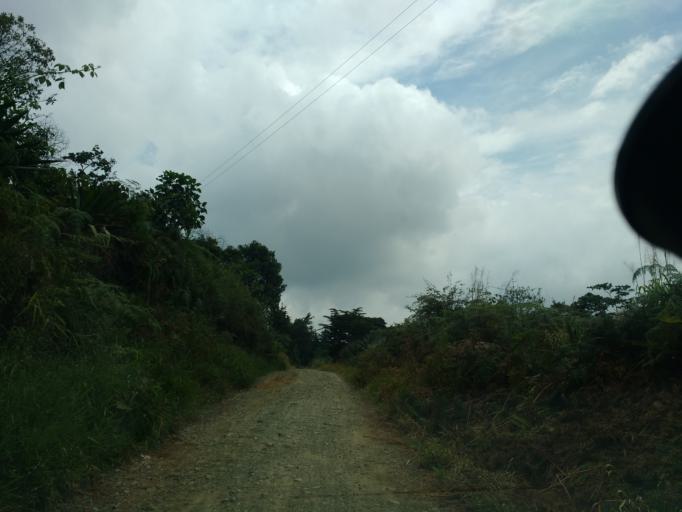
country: CO
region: Cauca
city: Santander de Quilichao
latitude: 2.9164
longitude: -76.4764
